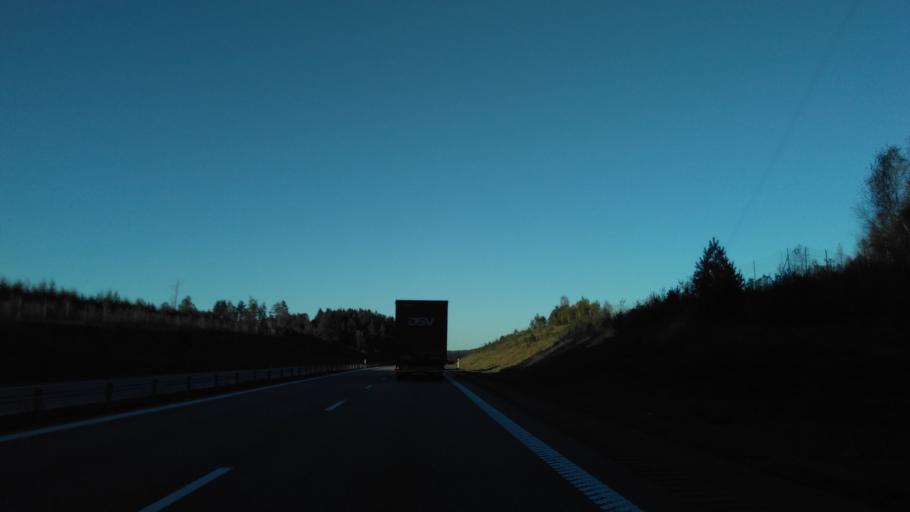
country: SE
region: Vaestra Goetaland
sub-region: Boras Kommun
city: Dalsjofors
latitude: 57.7760
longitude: 13.1164
